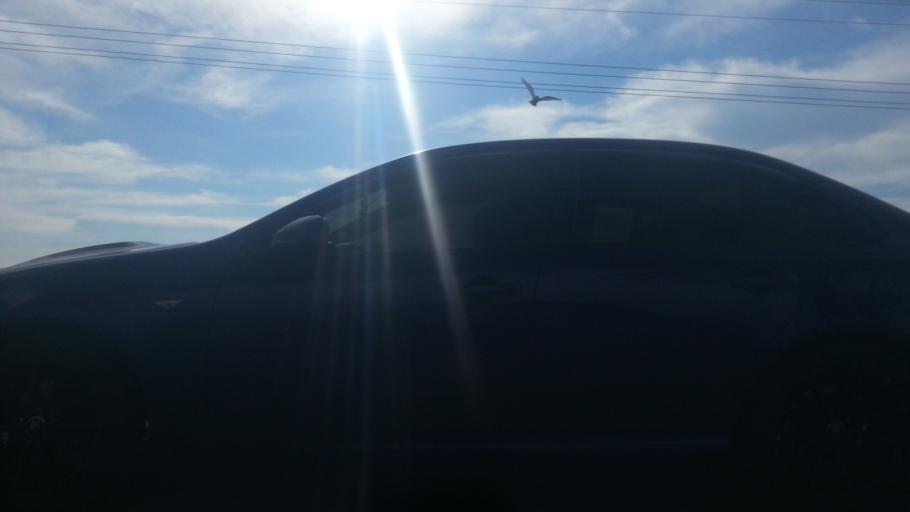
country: AU
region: New South Wales
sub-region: Liverpool
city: Luddenham
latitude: -33.8624
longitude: 150.6980
